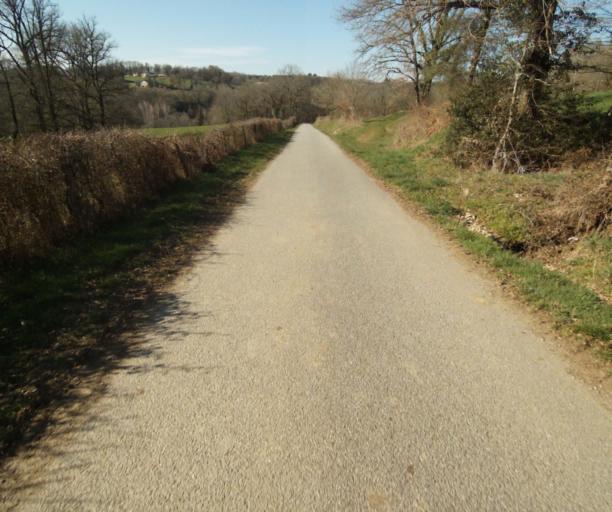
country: FR
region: Limousin
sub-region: Departement de la Correze
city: Chamboulive
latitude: 45.4823
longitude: 1.6866
